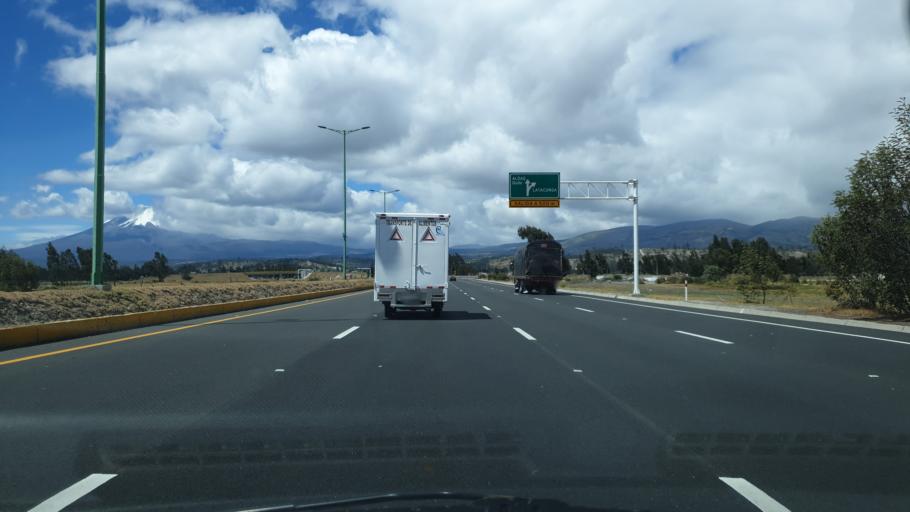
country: EC
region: Cotopaxi
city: Saquisili
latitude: -0.8690
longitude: -78.6328
